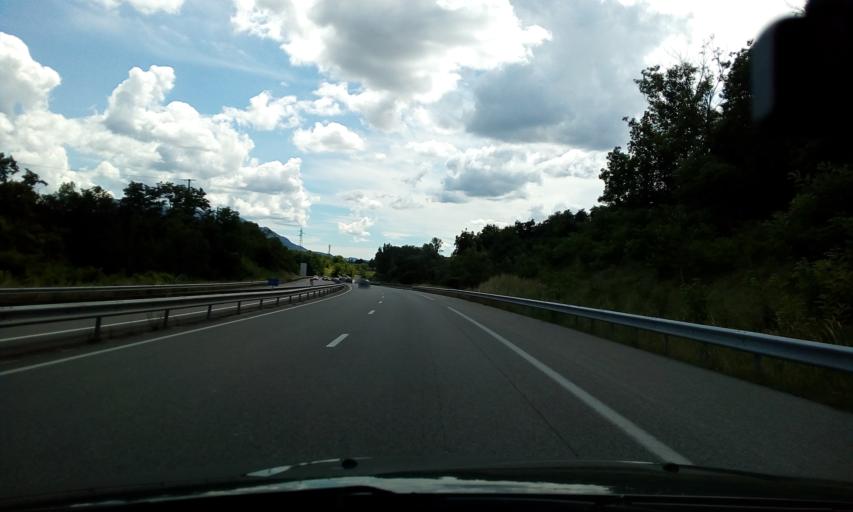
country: FR
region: Rhone-Alpes
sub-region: Departement de l'Isere
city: Saint-Hilaire-du-Rosier
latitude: 45.1125
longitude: 5.2575
